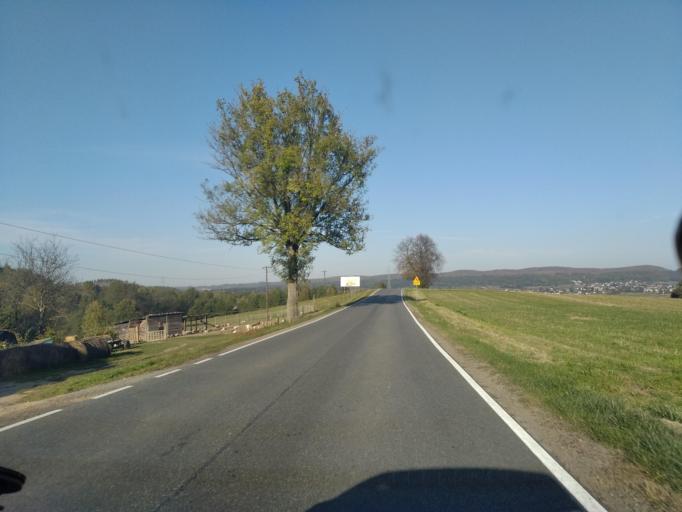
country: PL
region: Subcarpathian Voivodeship
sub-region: Powiat brzozowski
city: Turze Pole
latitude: 49.6669
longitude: 22.0190
